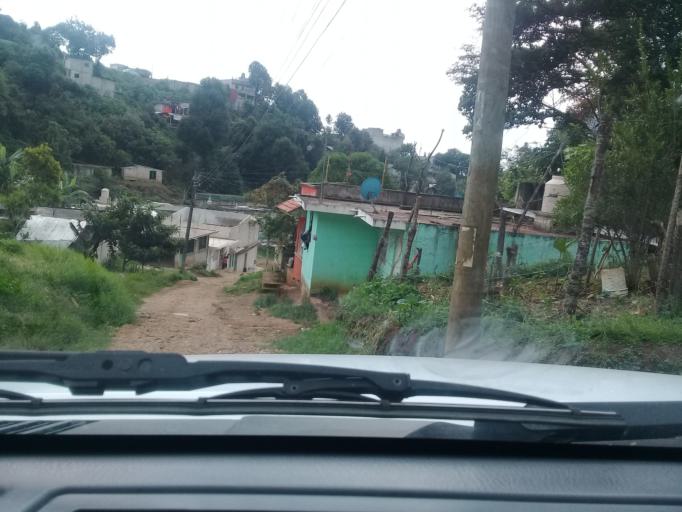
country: MX
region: Veracruz
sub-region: Tlalnelhuayocan
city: Guadalupe Victoria
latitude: 19.5584
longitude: -96.9573
